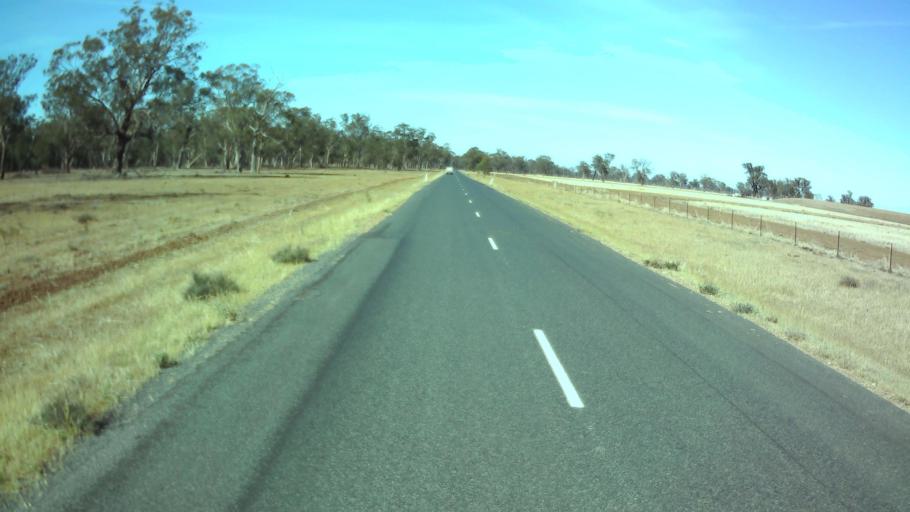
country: AU
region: New South Wales
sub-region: Weddin
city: Grenfell
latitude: -34.1288
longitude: 147.7988
